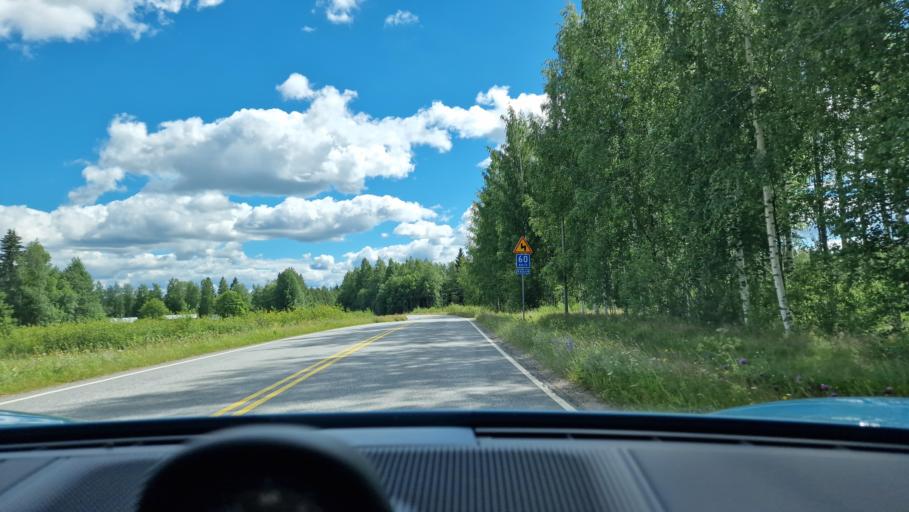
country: FI
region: Southern Ostrobothnia
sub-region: Jaerviseutu
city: Soini
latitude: 62.8305
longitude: 24.3384
